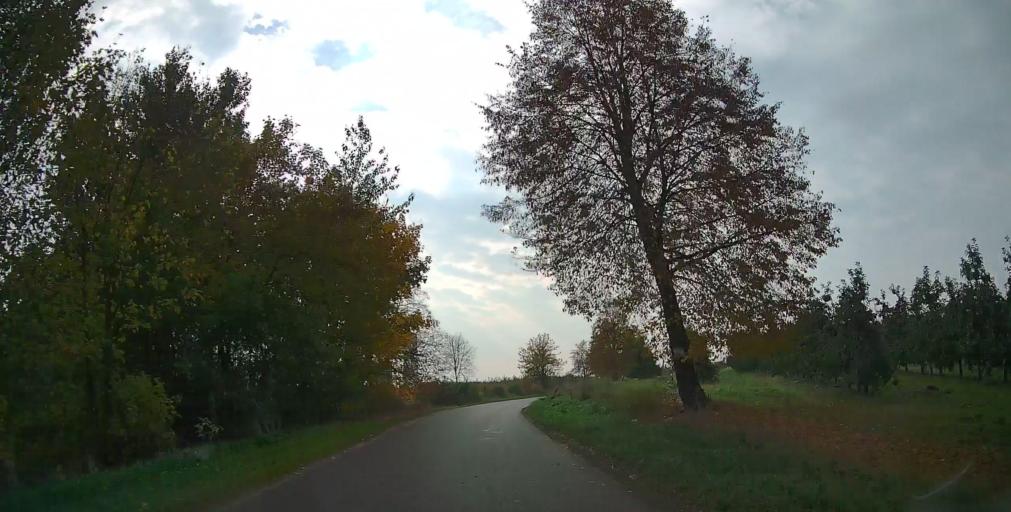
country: PL
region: Masovian Voivodeship
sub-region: Powiat grojecki
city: Mogielnica
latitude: 51.6808
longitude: 20.7143
